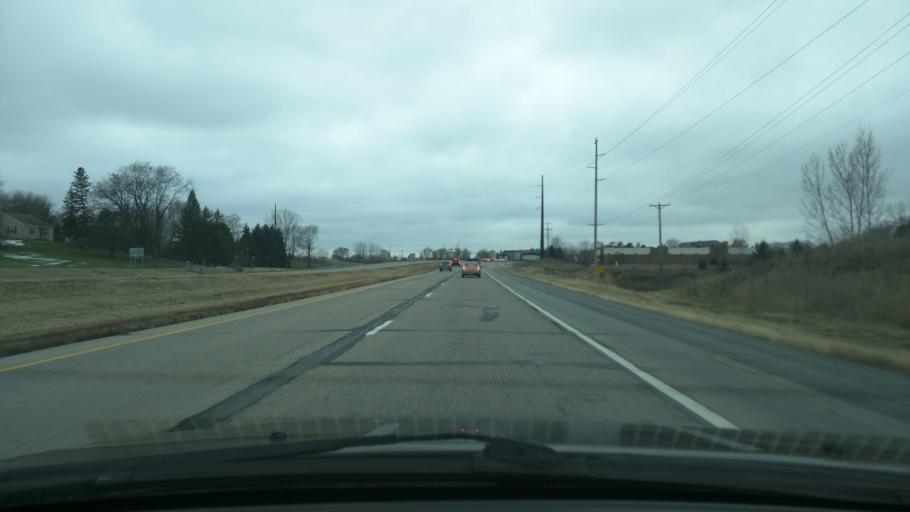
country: US
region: Minnesota
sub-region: Dakota County
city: Mendota Heights
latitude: 44.8452
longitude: -93.1184
